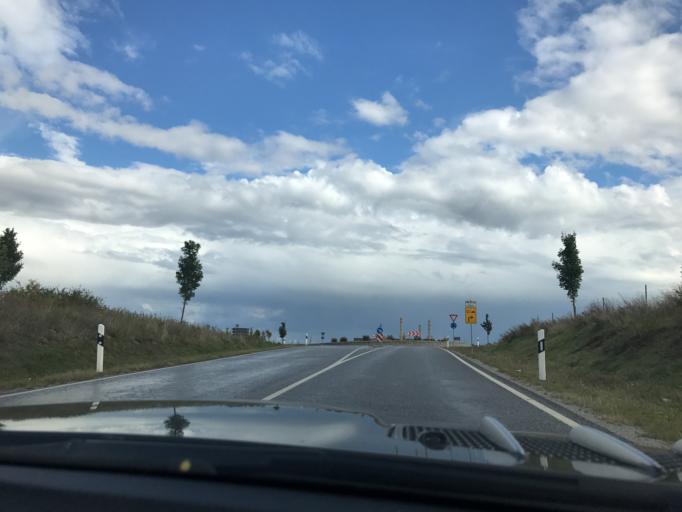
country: DE
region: Thuringia
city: Bad Langensalza
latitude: 51.0917
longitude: 10.6413
